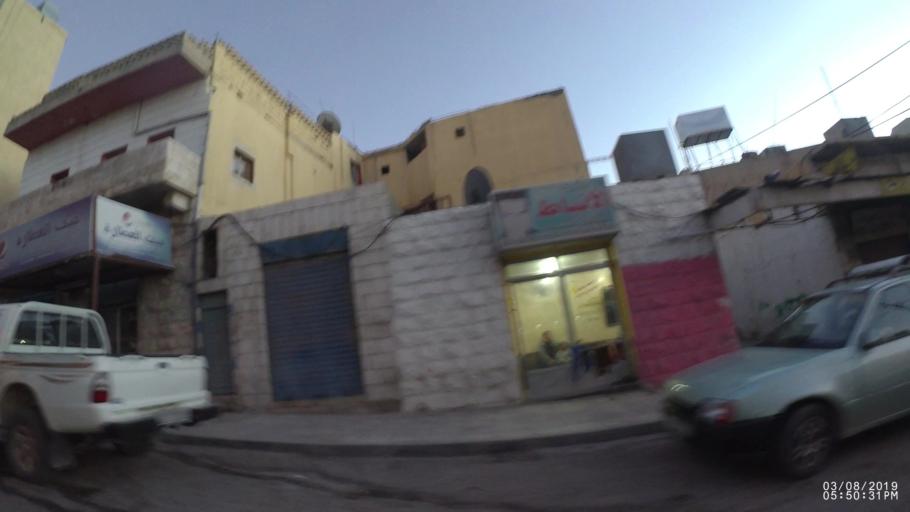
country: JO
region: Ma'an
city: Petra
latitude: 30.3207
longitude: 35.4794
